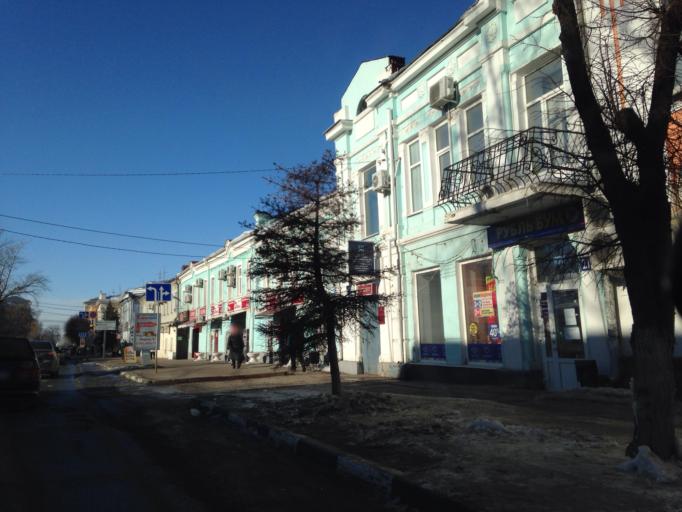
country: RU
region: Ulyanovsk
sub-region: Ulyanovskiy Rayon
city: Ulyanovsk
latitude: 54.3205
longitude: 48.3927
